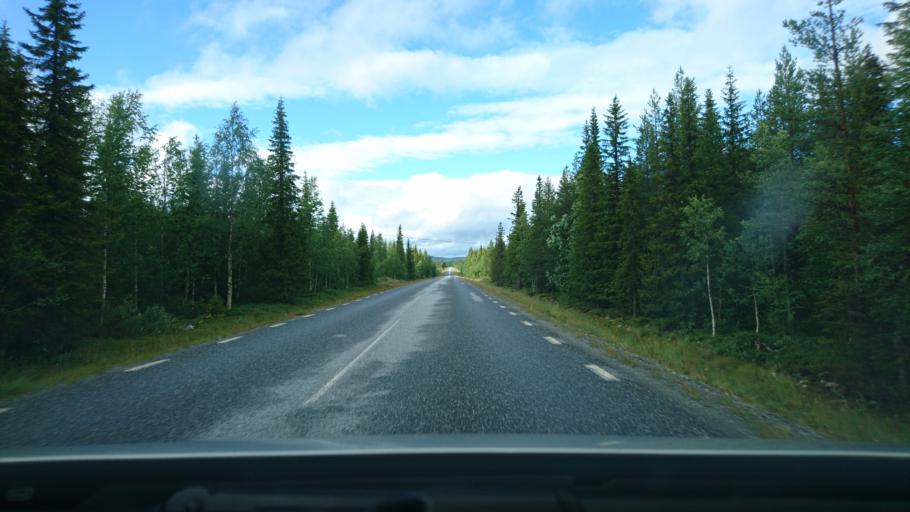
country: SE
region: Vaesterbotten
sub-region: Storumans Kommun
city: Storuman
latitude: 64.8651
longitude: 16.9918
